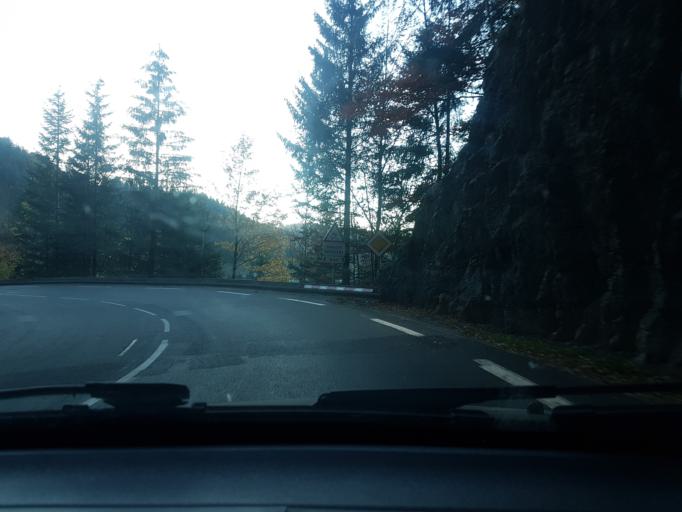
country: CH
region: Neuchatel
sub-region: Le Locle District
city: Les Brenets
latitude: 47.0515
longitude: 6.7190
